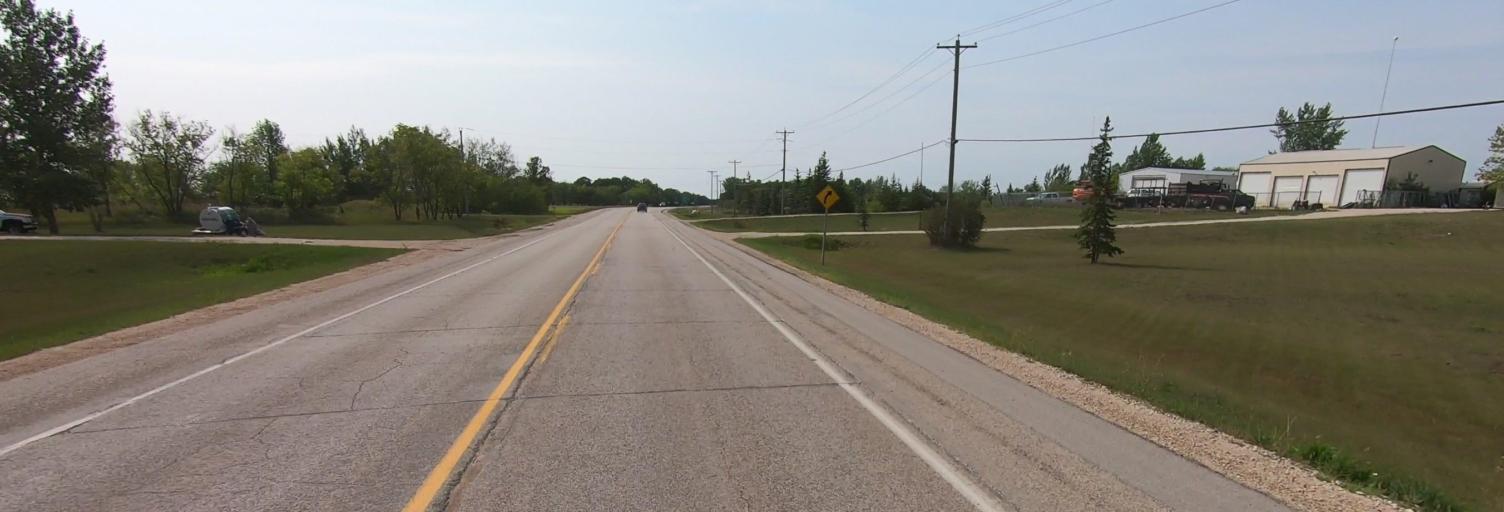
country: CA
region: Manitoba
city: Niverville
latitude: 49.7122
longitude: -97.0904
